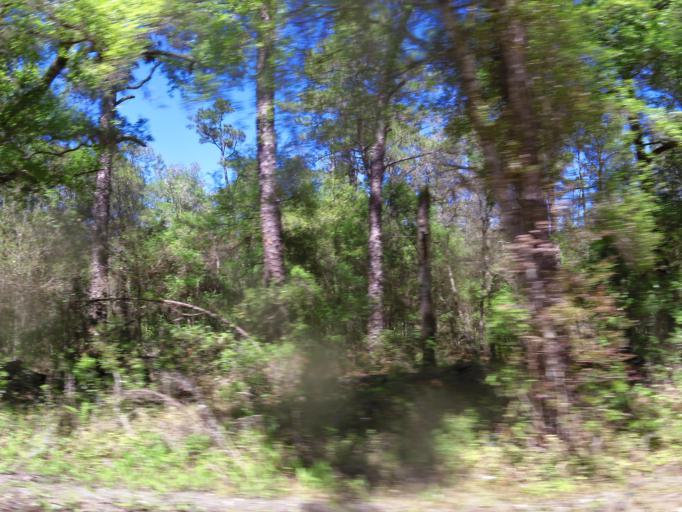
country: US
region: Florida
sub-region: Bradford County
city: Starke
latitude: 30.0468
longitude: -82.0610
